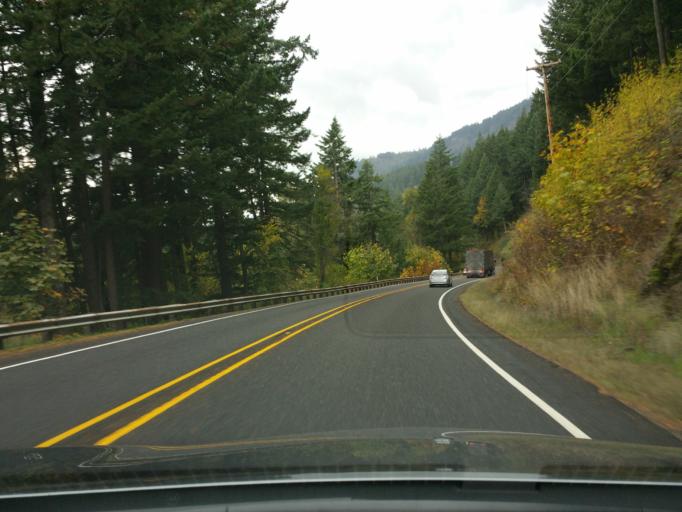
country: US
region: Oregon
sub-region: Hood River County
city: Cascade Locks
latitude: 45.6024
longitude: -122.1036
